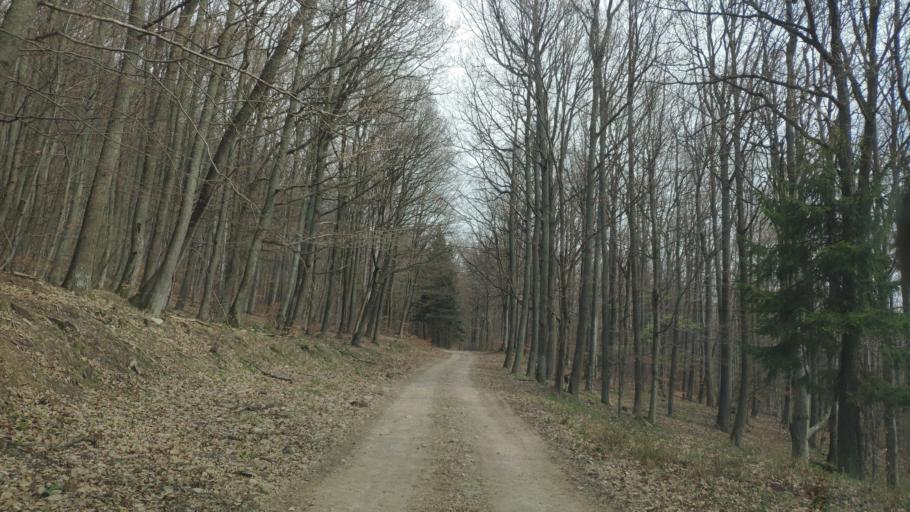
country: SK
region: Kosicky
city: Moldava nad Bodvou
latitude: 48.7430
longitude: 21.0373
